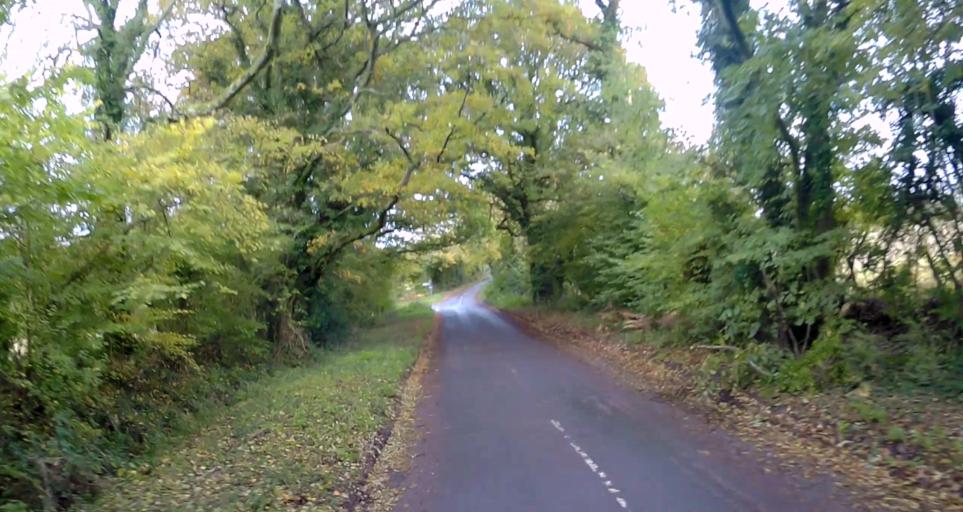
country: GB
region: England
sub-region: Hampshire
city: Four Marks
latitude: 51.1506
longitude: -1.0880
